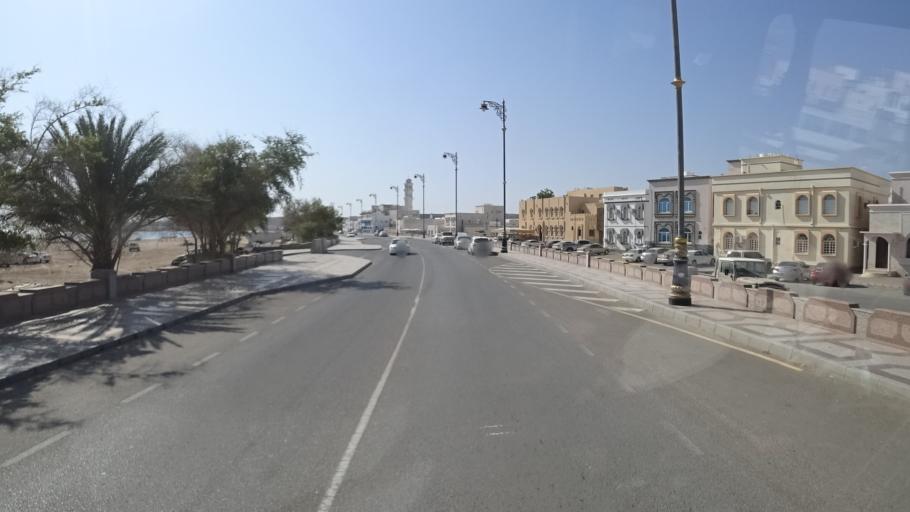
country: OM
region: Ash Sharqiyah
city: Sur
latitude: 22.5720
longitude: 59.5285
